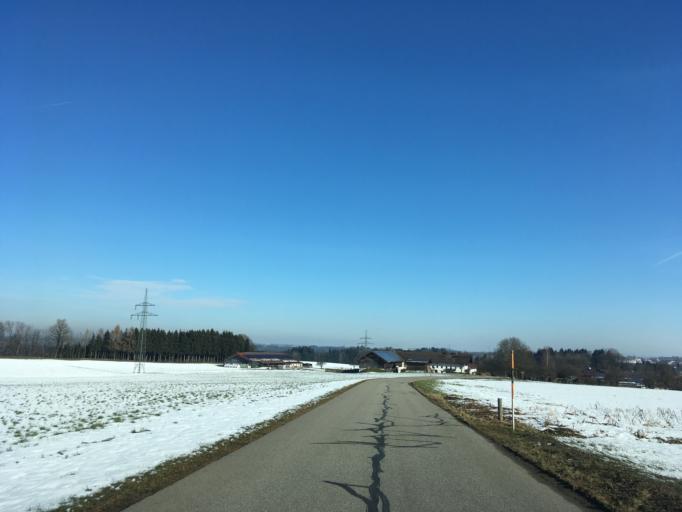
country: DE
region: Bavaria
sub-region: Upper Bavaria
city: Vogtareuth
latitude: 47.9271
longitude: 12.1604
